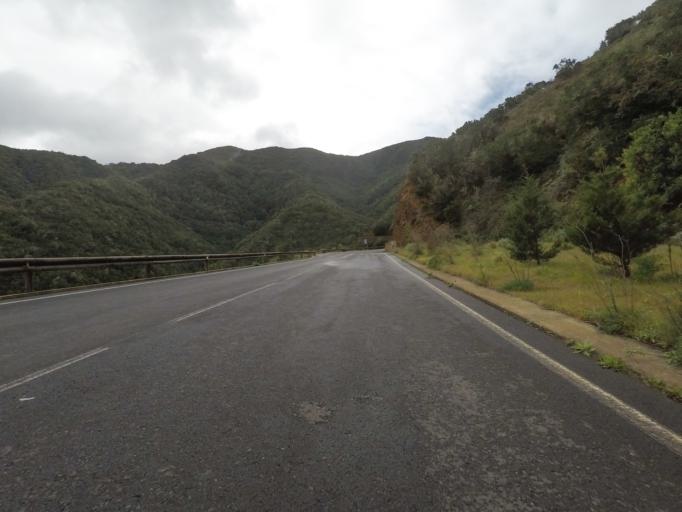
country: ES
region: Canary Islands
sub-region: Provincia de Santa Cruz de Tenerife
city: Vallehermosa
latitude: 28.1585
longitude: -17.2863
